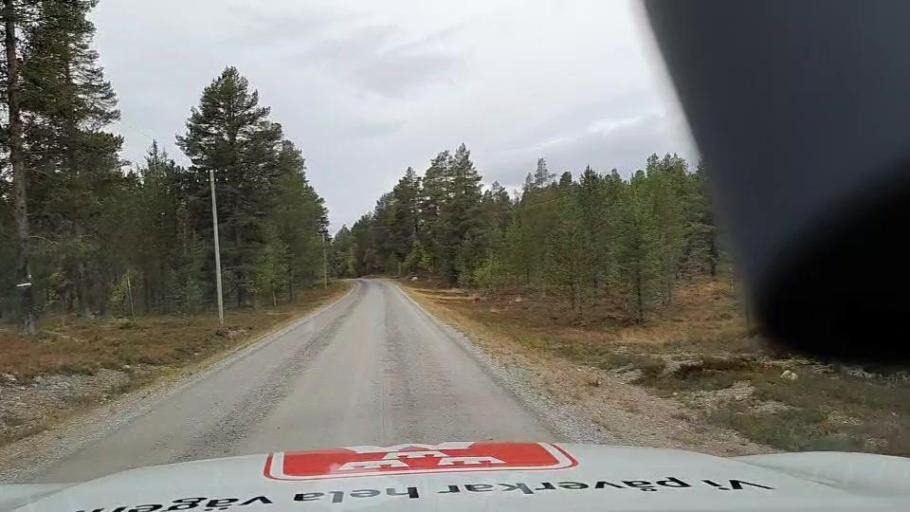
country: NO
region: Hedmark
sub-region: Engerdal
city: Engerdal
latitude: 62.0919
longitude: 12.7771
